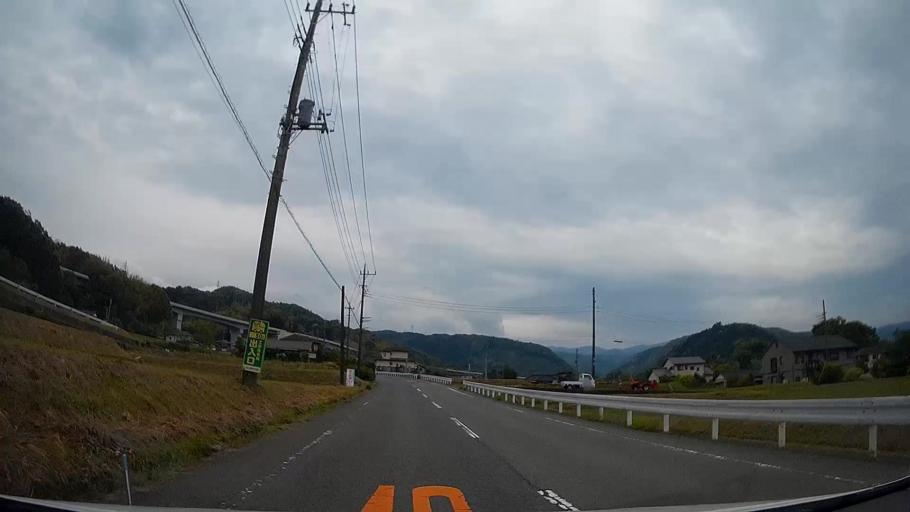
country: JP
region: Shizuoka
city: Ito
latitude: 34.9281
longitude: 138.9357
